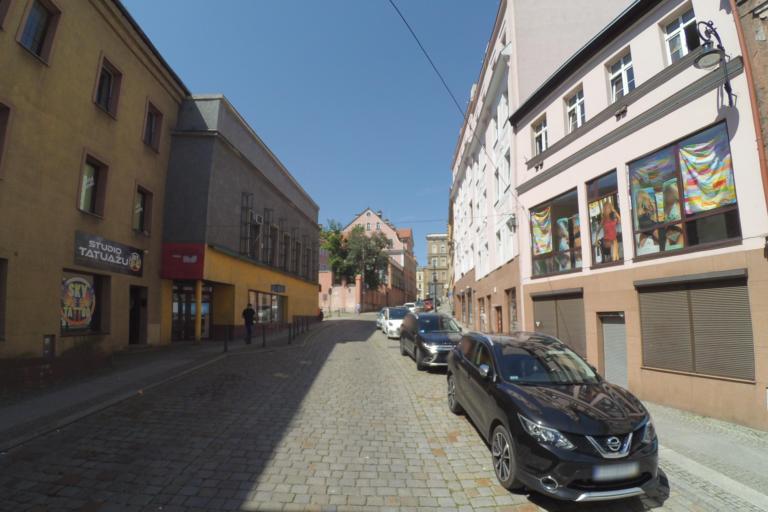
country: PL
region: Lower Silesian Voivodeship
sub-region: Powiat walbrzyski
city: Walbrzych
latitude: 50.7664
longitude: 16.2846
